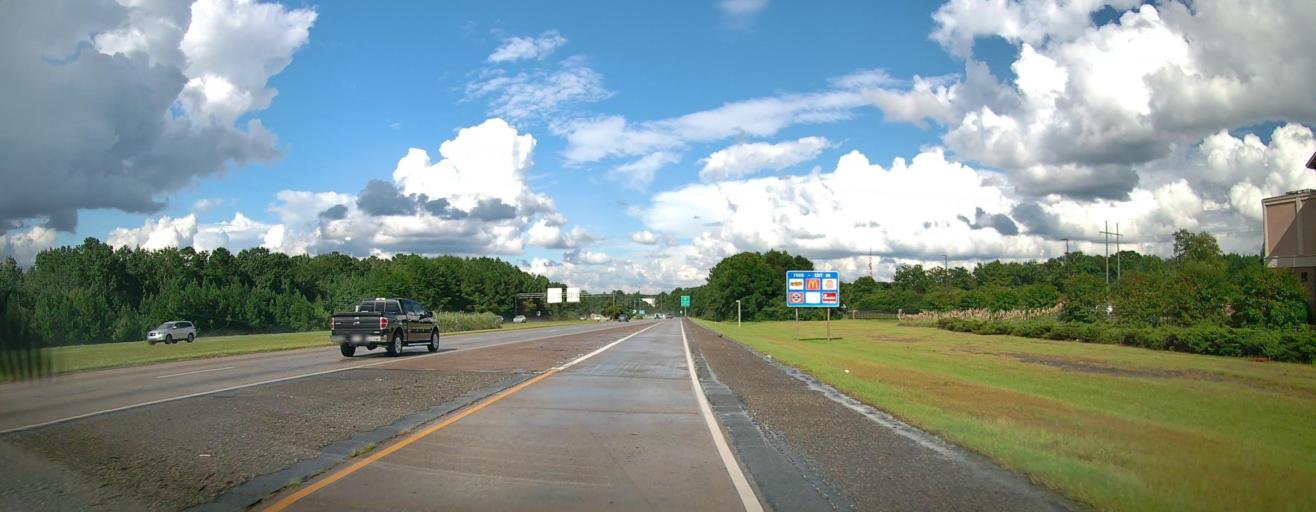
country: US
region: Alabama
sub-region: Russell County
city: Phenix City
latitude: 32.5233
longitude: -84.9845
